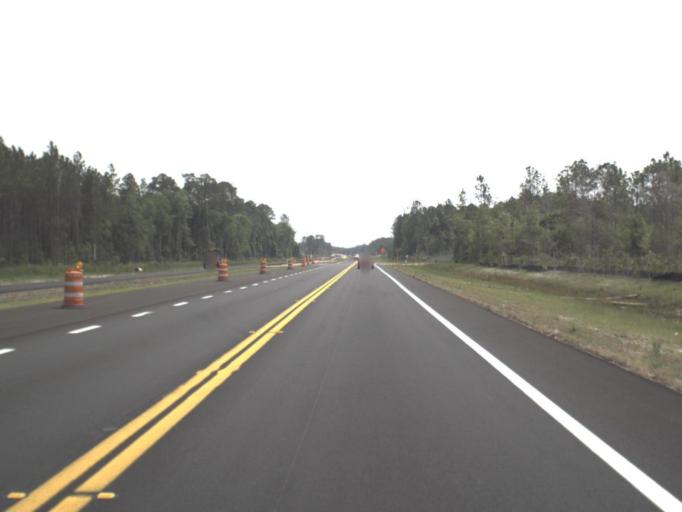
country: US
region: Florida
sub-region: Nassau County
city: Nassau Village-Ratliff
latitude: 30.4901
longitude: -81.8917
